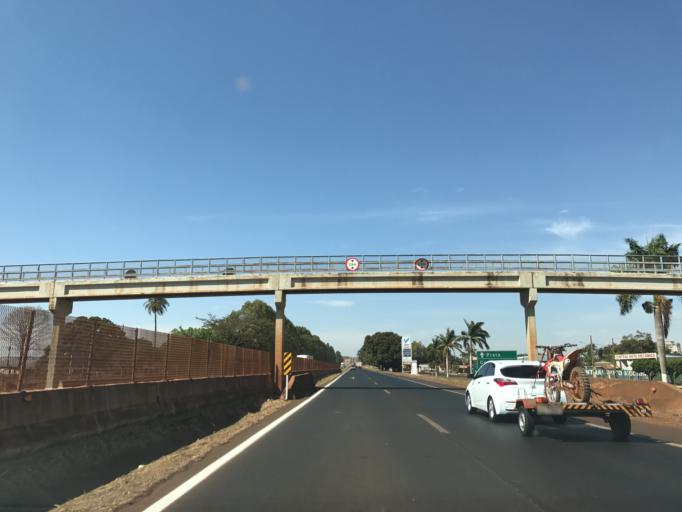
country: BR
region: Minas Gerais
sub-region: Centralina
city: Centralina
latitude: -18.5813
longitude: -49.1933
